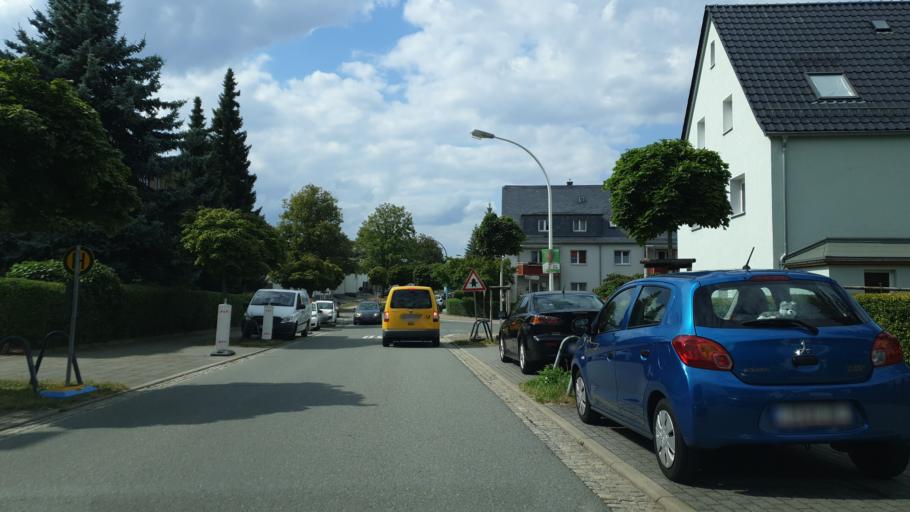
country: DE
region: Saxony
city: Neukirchen
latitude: 50.8087
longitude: 12.8345
